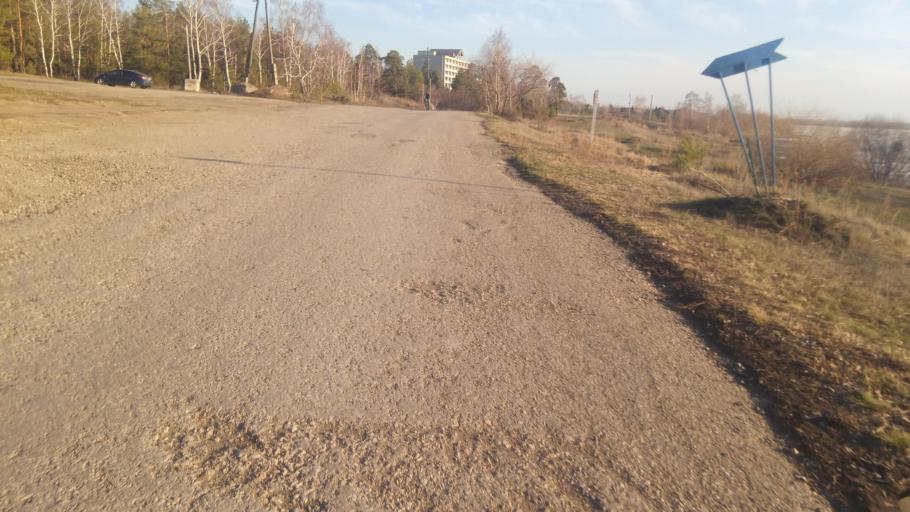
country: RU
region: Chelyabinsk
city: Novosineglazovskiy
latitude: 55.1275
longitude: 61.3283
